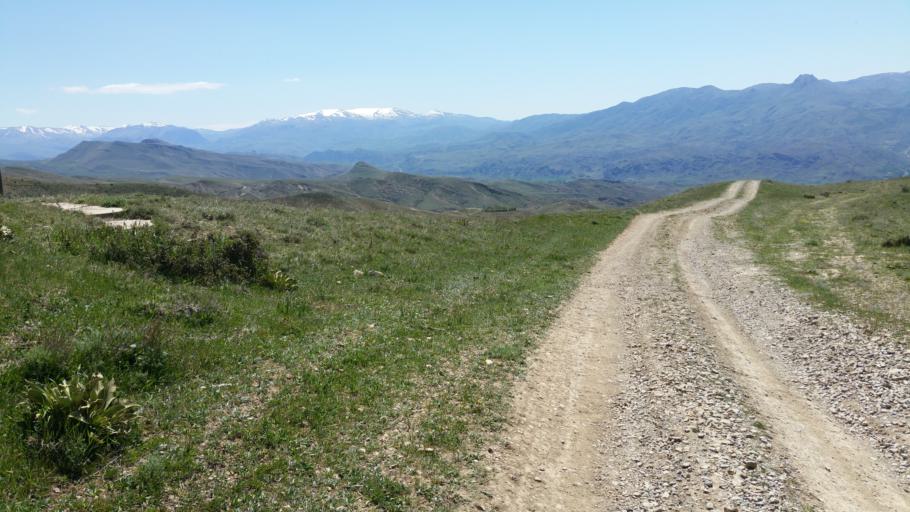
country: AM
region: Vayots' Dzori Marz
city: Vernashen
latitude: 39.8024
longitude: 45.3604
